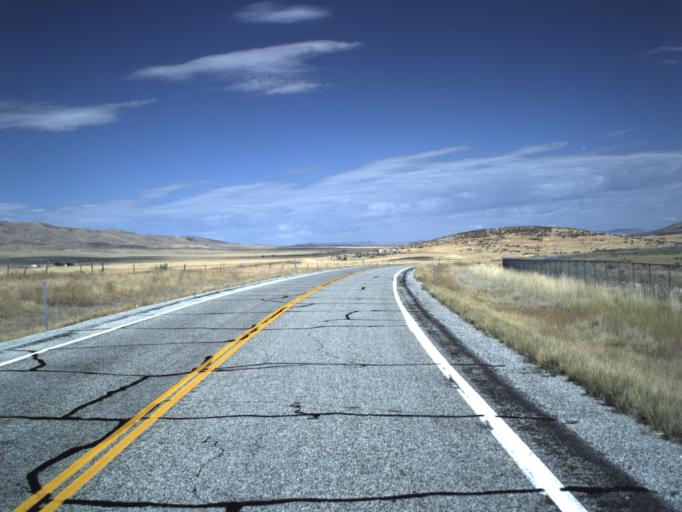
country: US
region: Utah
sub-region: Box Elder County
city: Tremonton
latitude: 41.7104
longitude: -112.4521
